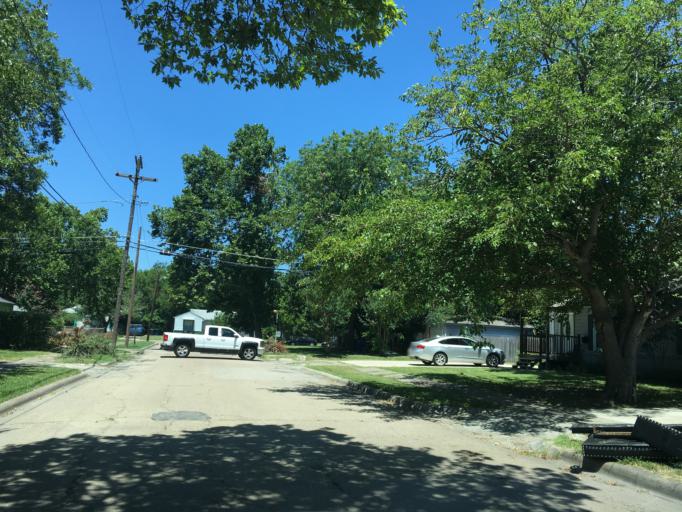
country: US
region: Texas
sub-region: Dallas County
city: Garland
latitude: 32.8445
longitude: -96.6766
